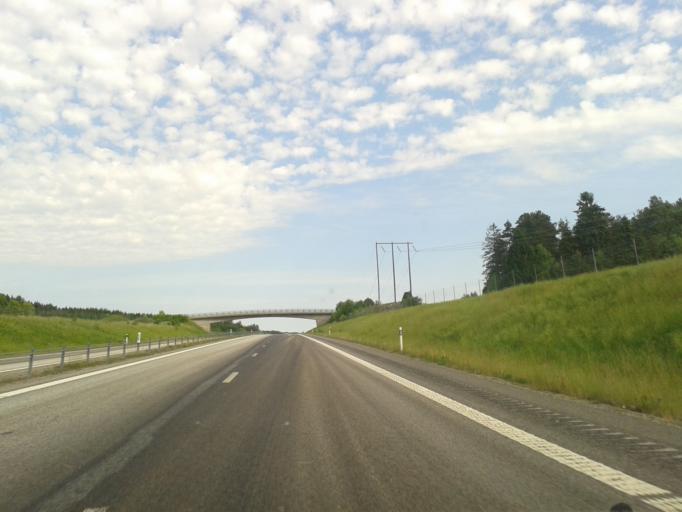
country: SE
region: Vaestra Goetaland
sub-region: Munkedals Kommun
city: Munkedal
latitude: 58.5052
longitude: 11.5626
